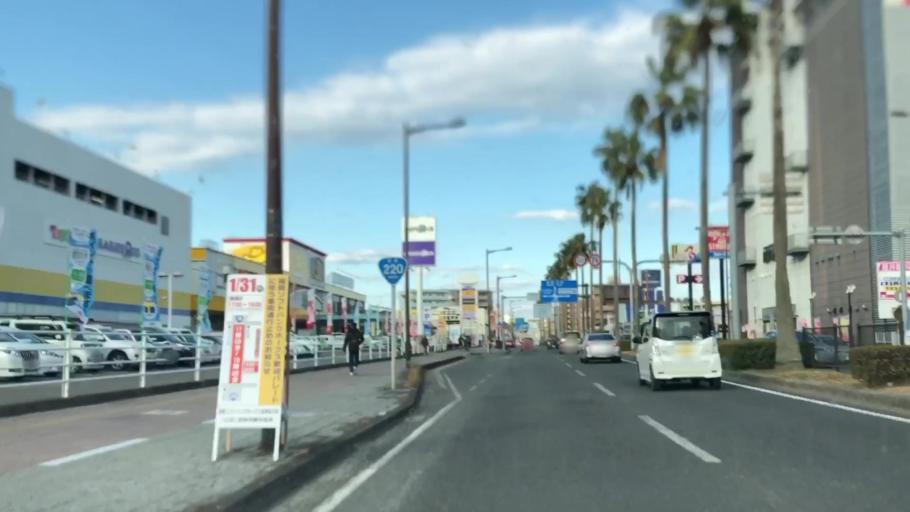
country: JP
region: Miyazaki
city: Miyazaki-shi
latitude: 31.8948
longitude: 131.4168
